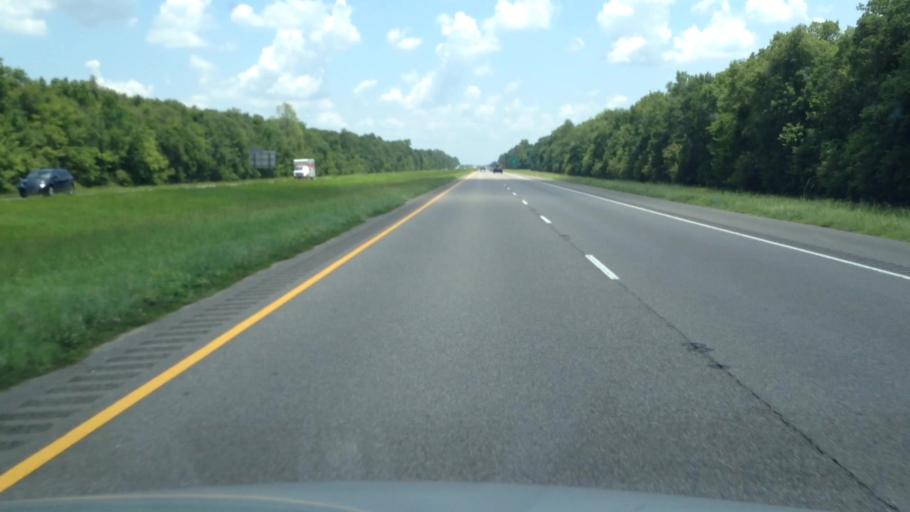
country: US
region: Louisiana
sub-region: Avoyelles Parish
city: Bunkie
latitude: 30.9725
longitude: -92.2933
